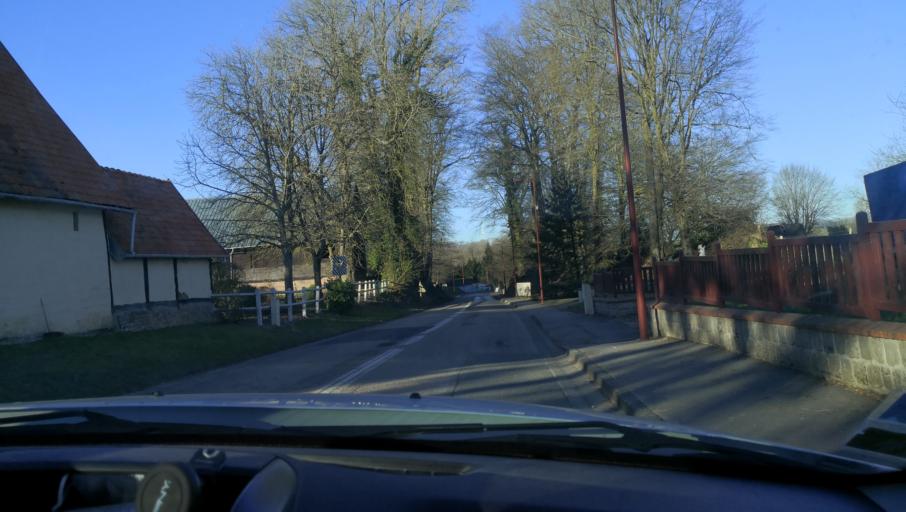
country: FR
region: Haute-Normandie
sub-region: Departement de la Seine-Maritime
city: Totes
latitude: 49.6651
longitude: 1.0253
